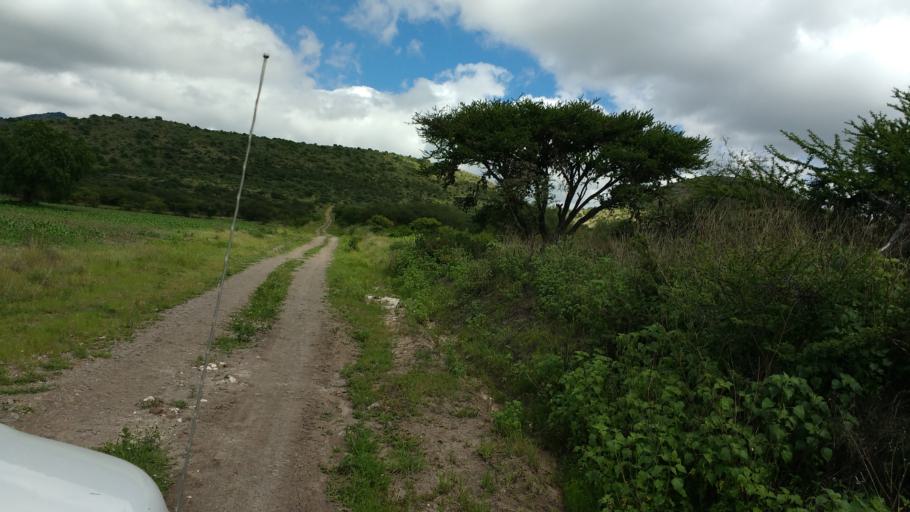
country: MX
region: Hidalgo
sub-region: Tezontepec de Aldama
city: Tenango
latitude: 20.2471
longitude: -99.2724
